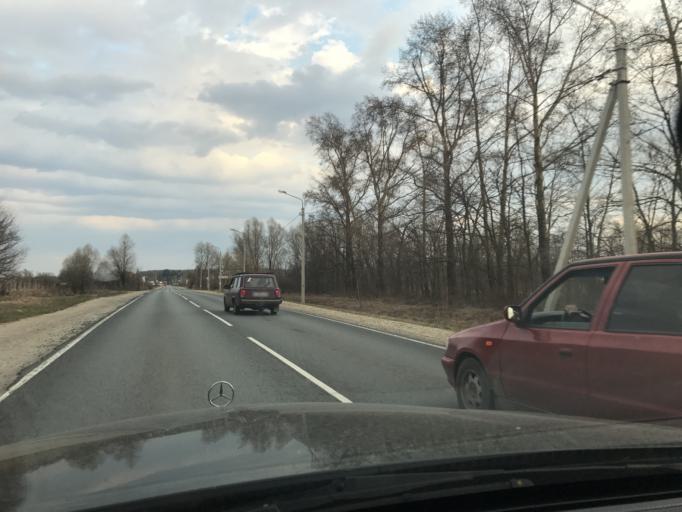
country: RU
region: Vladimir
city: Murom
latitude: 55.6412
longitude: 41.8489
